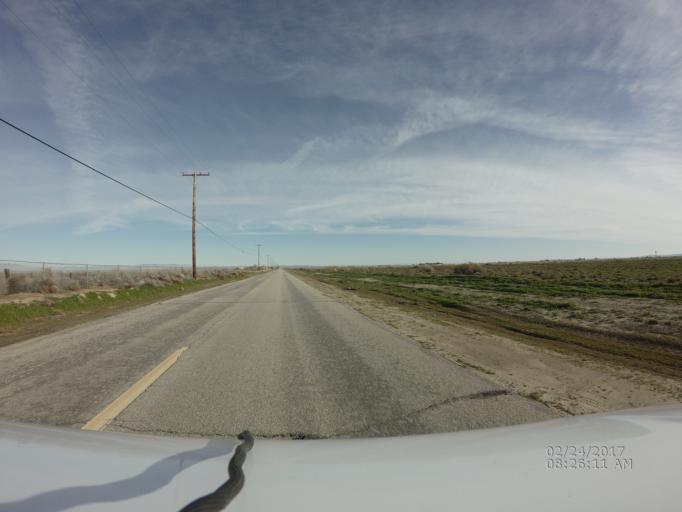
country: US
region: California
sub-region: Los Angeles County
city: Lancaster
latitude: 34.7207
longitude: -118.0233
